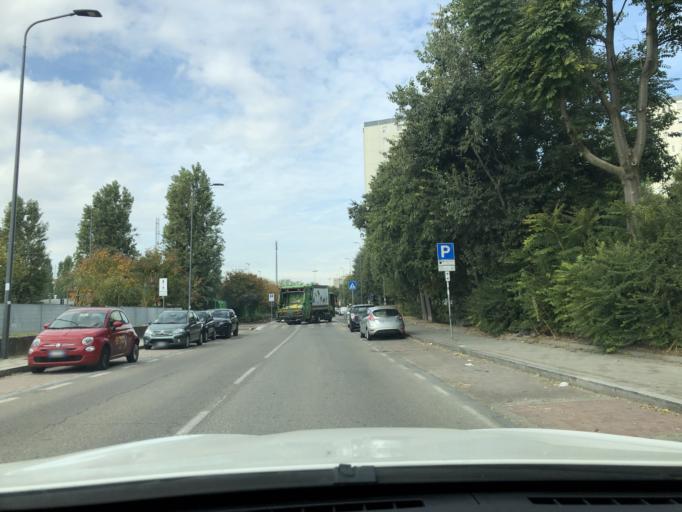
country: IT
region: Lombardy
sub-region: Citta metropolitana di Milano
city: Pero
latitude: 45.4994
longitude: 9.1059
